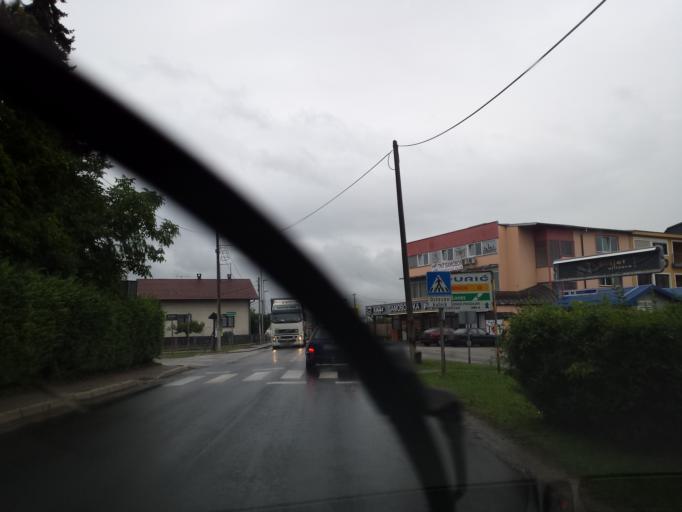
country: HR
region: Zagrebacka
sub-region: Grad Samobor
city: Samobor
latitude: 45.8058
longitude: 15.7182
